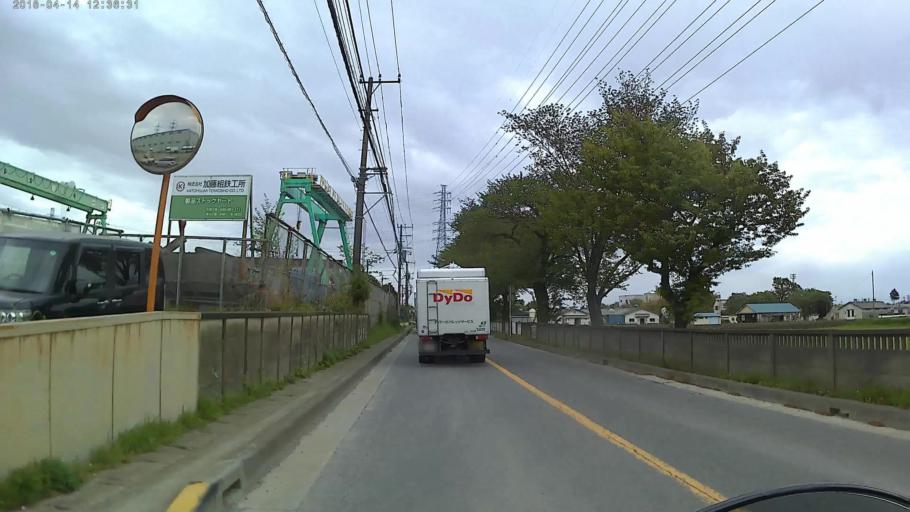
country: JP
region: Kanagawa
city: Atsugi
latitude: 35.4156
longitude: 139.4075
